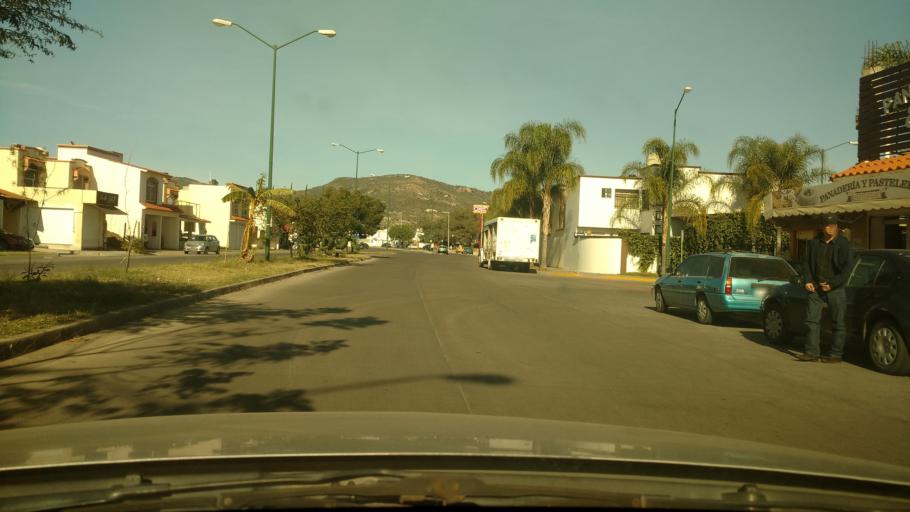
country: MX
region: Guanajuato
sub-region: Leon
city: Medina
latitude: 21.1701
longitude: -101.6514
